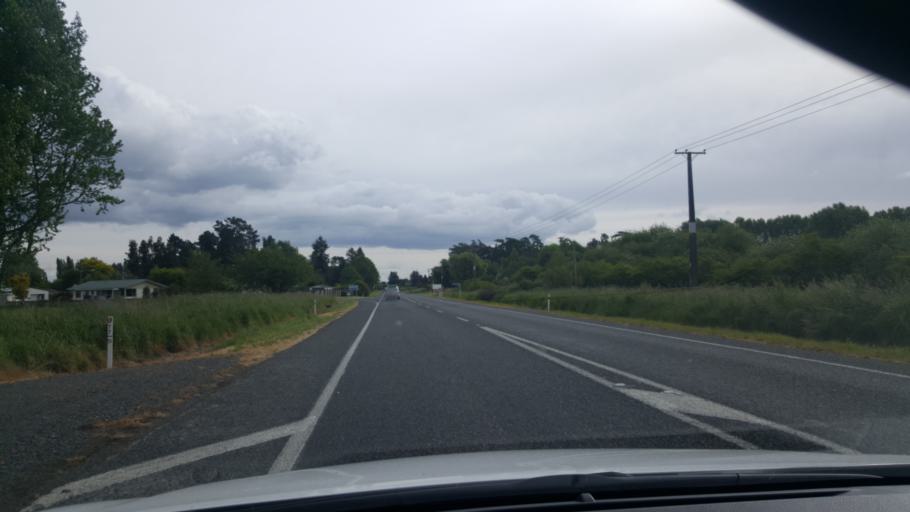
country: NZ
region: Waikato
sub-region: Taupo District
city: Taupo
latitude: -38.4664
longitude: 176.3118
